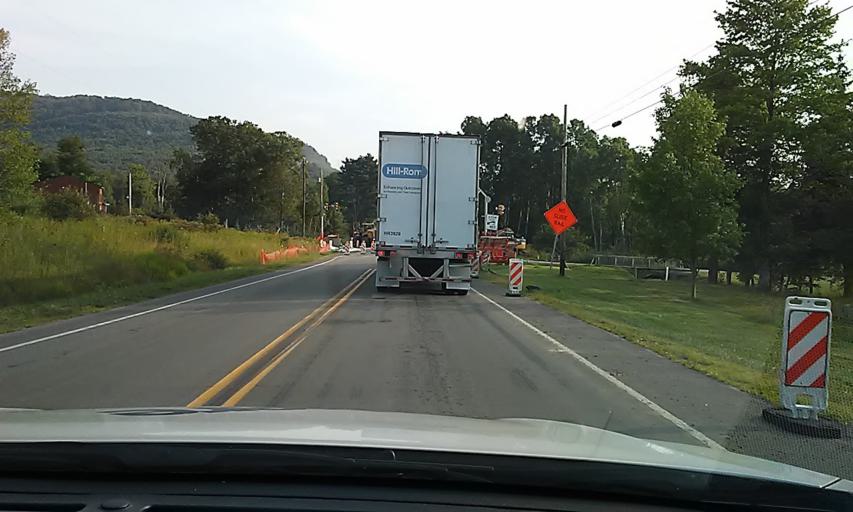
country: US
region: Pennsylvania
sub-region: McKean County
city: Smethport
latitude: 41.7510
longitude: -78.5259
